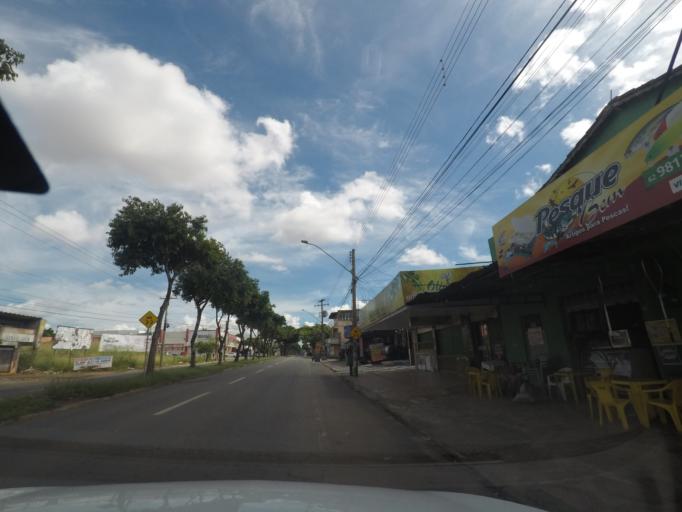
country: BR
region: Goias
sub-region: Goiania
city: Goiania
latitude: -16.7238
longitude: -49.3224
